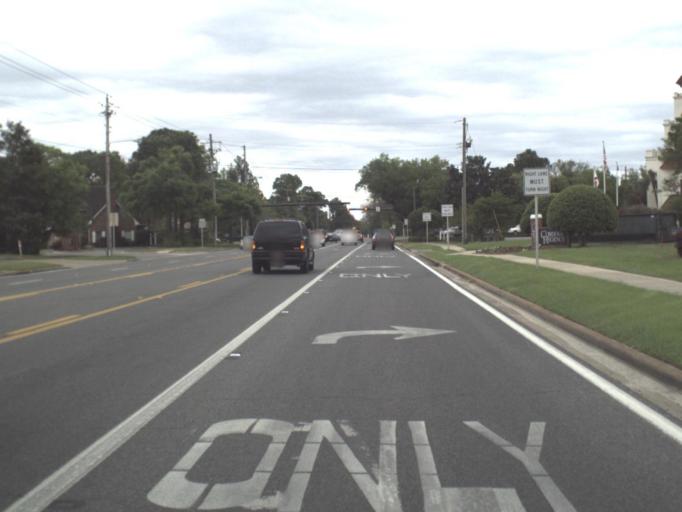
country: US
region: Florida
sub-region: Escambia County
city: Goulding
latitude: 30.4668
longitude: -87.2050
